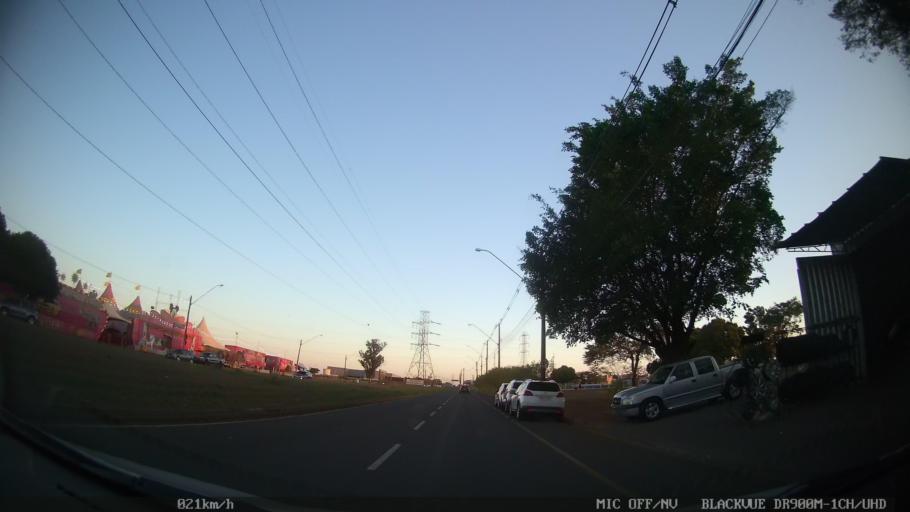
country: BR
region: Sao Paulo
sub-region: Sao Jose Do Rio Preto
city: Sao Jose do Rio Preto
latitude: -20.7944
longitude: -49.3450
